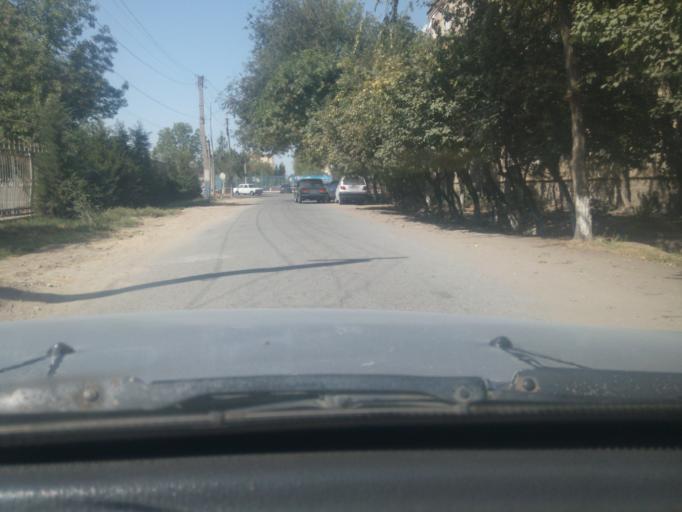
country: UZ
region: Sirdaryo
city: Guliston
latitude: 40.5012
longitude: 68.7765
